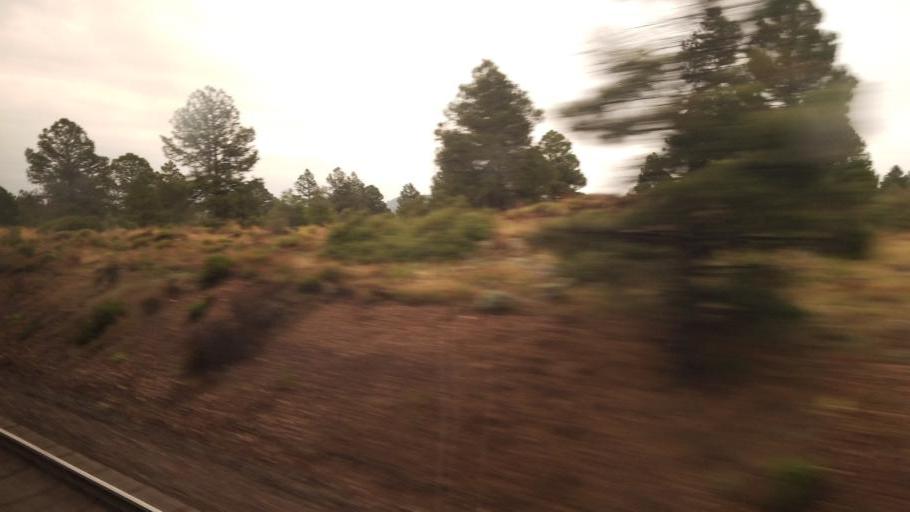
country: US
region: Arizona
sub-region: Coconino County
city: Parks
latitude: 35.2407
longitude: -111.9780
